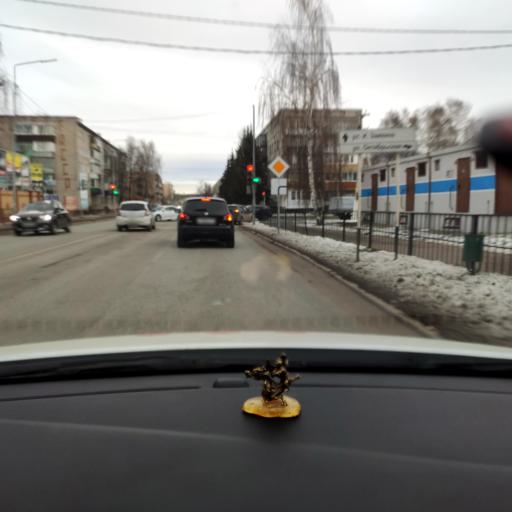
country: RU
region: Tatarstan
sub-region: Zelenodol'skiy Rayon
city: Zelenodolsk
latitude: 55.8476
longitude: 48.5245
